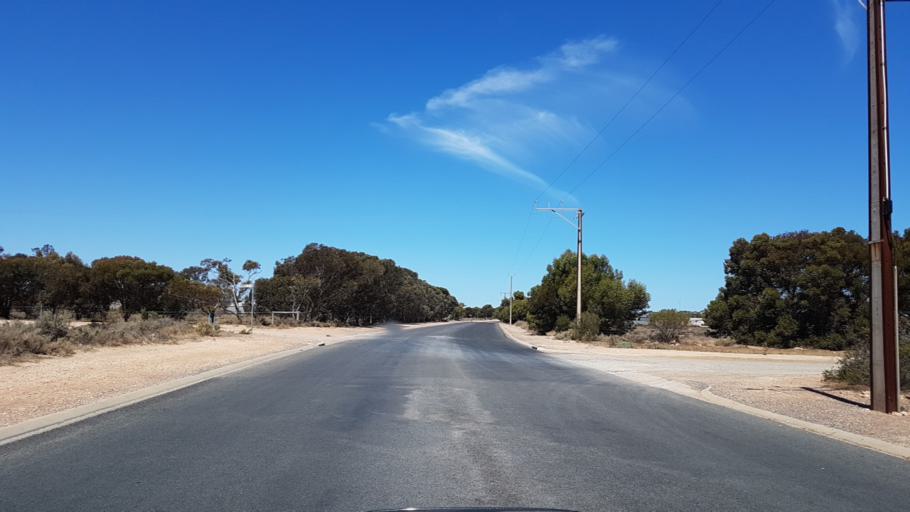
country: AU
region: South Australia
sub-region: Copper Coast
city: Wallaroo
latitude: -34.0528
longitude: 137.5768
